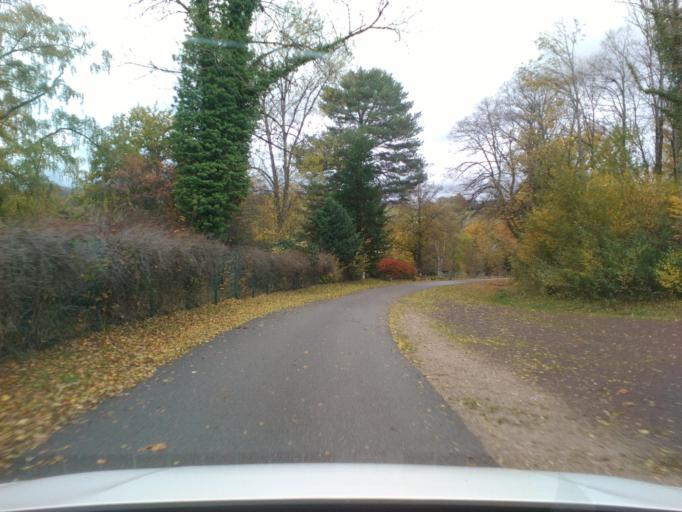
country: FR
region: Lorraine
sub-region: Departement des Vosges
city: Senones
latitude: 48.3398
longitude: 7.0150
